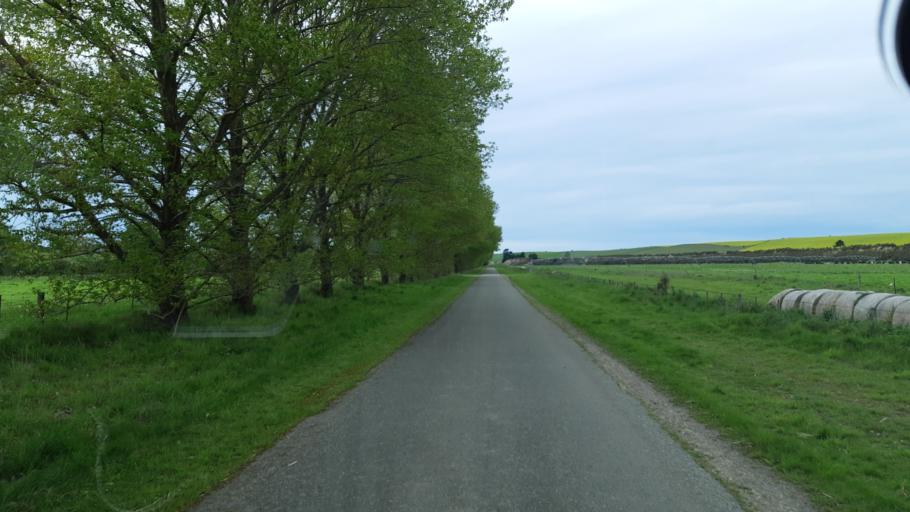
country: NZ
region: Canterbury
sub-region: Timaru District
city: Timaru
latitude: -44.5356
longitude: 171.1241
